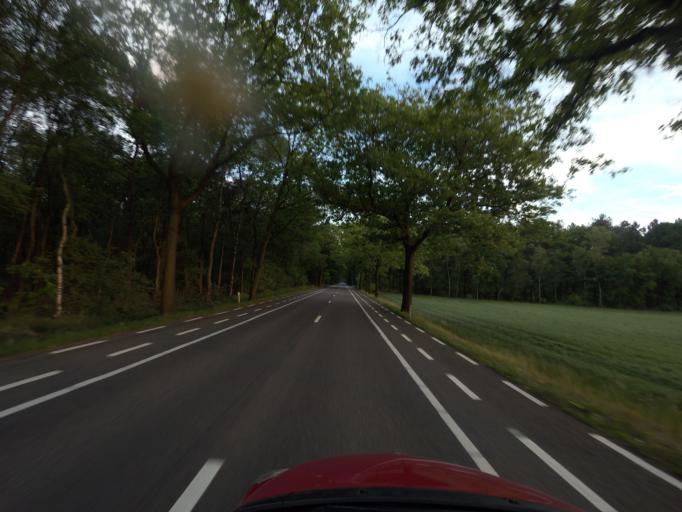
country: BE
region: Flanders
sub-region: Provincie Limburg
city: Overpelt
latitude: 51.1837
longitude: 5.3637
